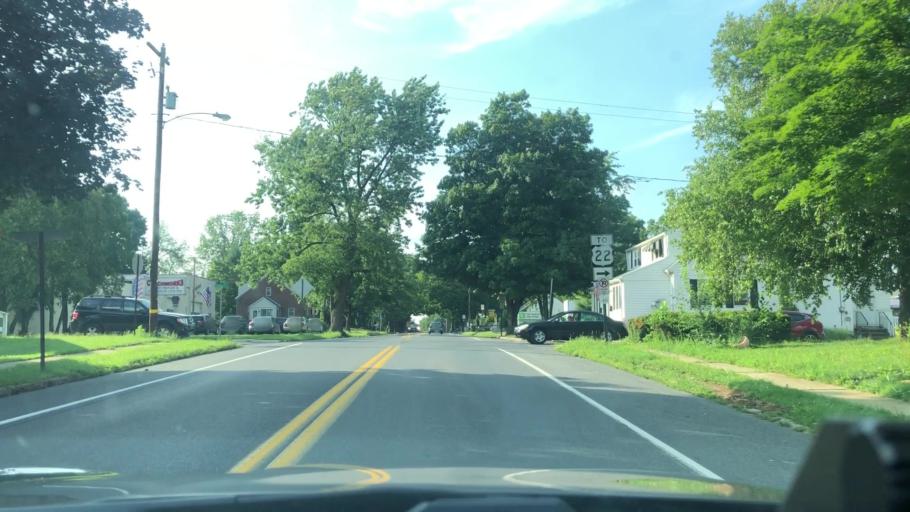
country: US
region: Pennsylvania
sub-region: Lehigh County
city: Allentown
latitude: 40.6190
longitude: -75.5052
